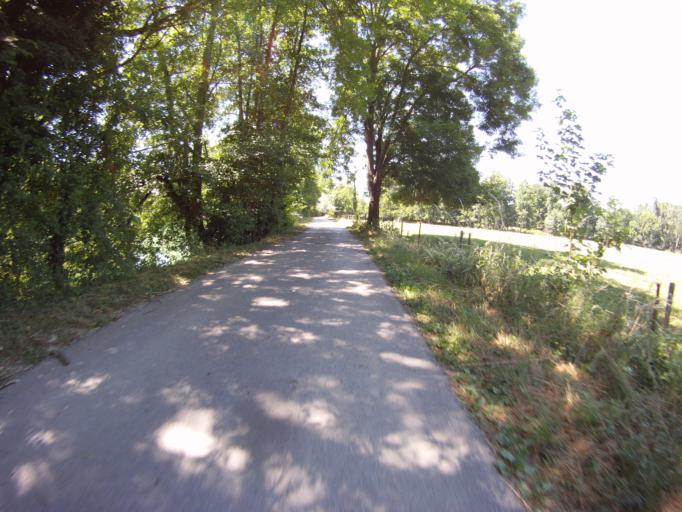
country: FR
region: Champagne-Ardenne
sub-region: Departement de la Marne
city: Damery
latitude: 49.0657
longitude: 3.8909
